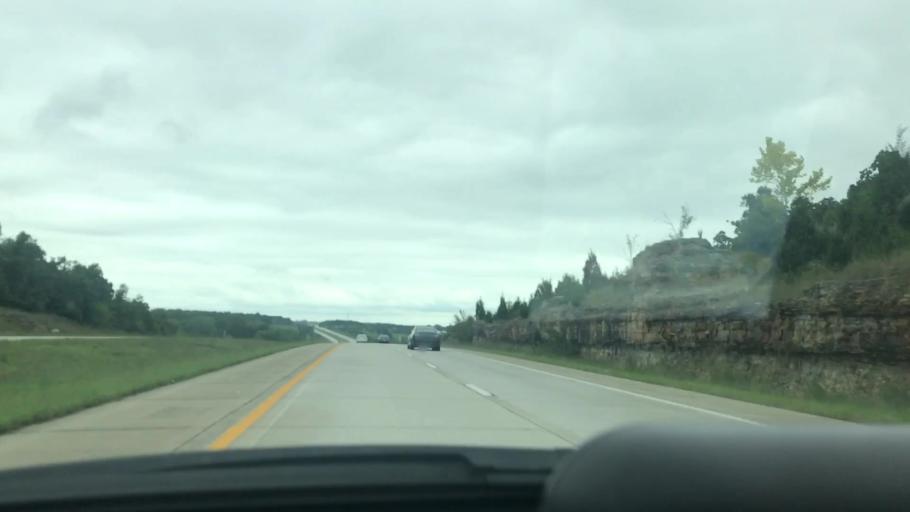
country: US
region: Missouri
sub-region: Dallas County
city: Buffalo
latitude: 37.5218
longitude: -93.1379
